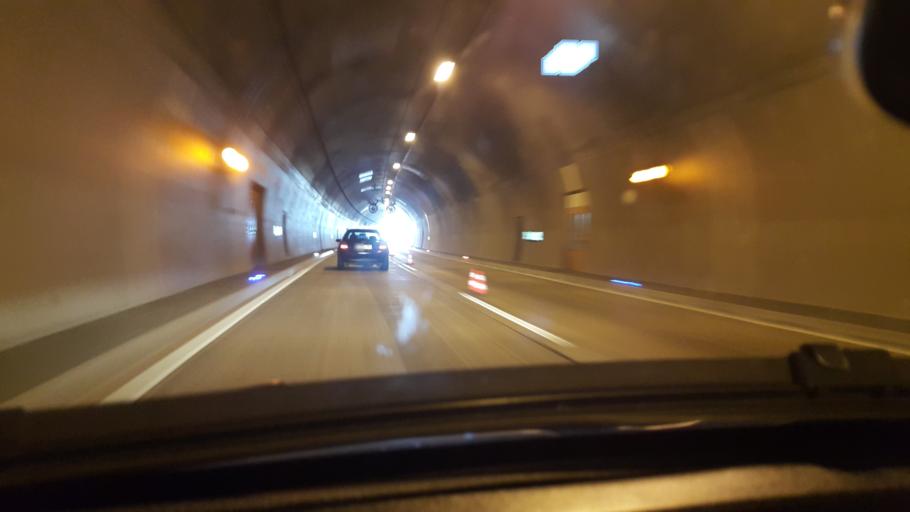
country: SI
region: Koper-Capodistria
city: Dekani
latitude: 45.5545
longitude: 13.8061
